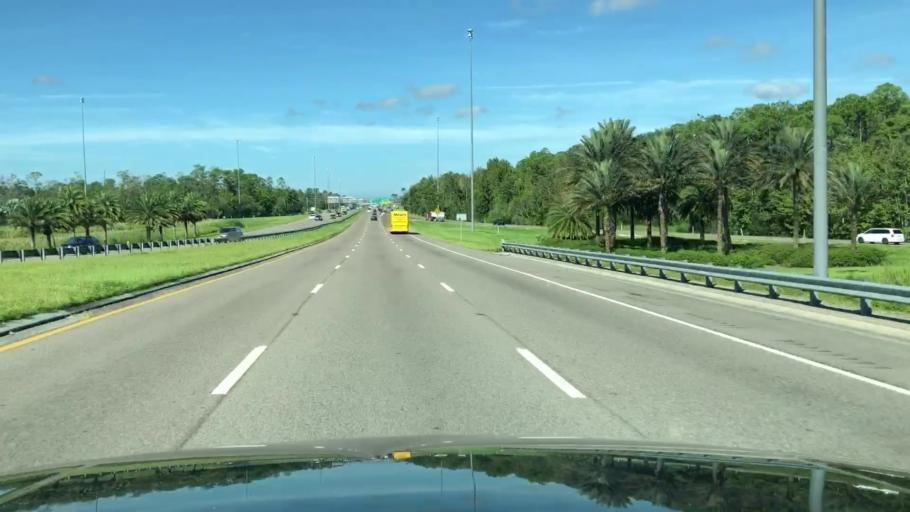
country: US
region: Florida
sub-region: Osceola County
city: Celebration
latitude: 28.3328
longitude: -81.5476
